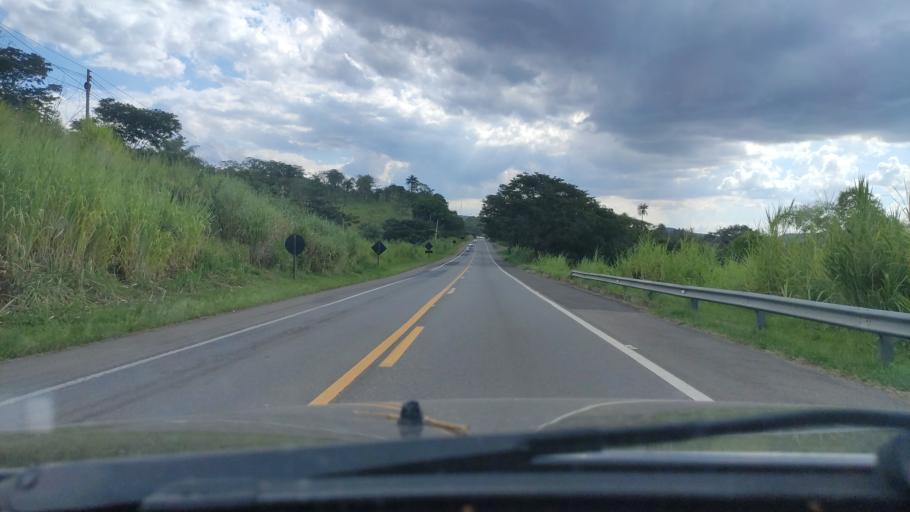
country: BR
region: Sao Paulo
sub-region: Aguas De Lindoia
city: Aguas de Lindoia
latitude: -22.4601
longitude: -46.7258
